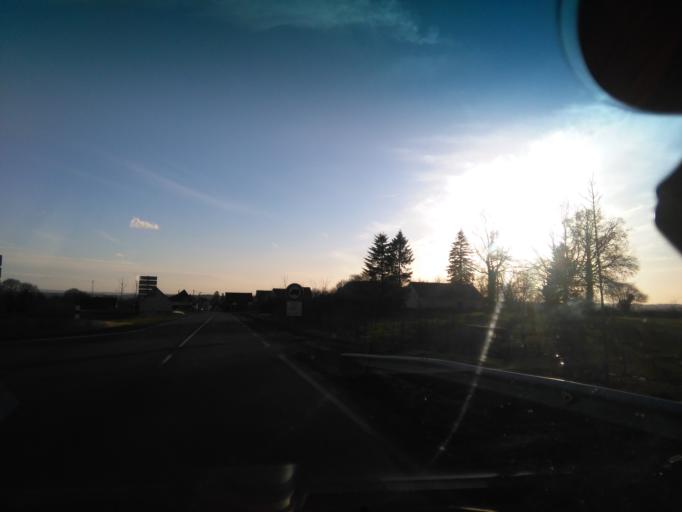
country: FR
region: Lower Normandy
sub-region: Departement de l'Orne
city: La Ferte-Mace
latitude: 48.6110
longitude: -0.3527
